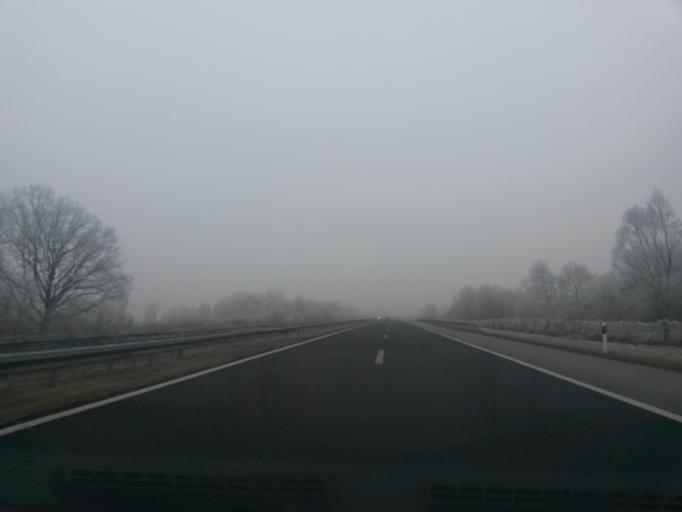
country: HR
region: Zagrebacka
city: Brckovljani
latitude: 45.9315
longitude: 16.2706
